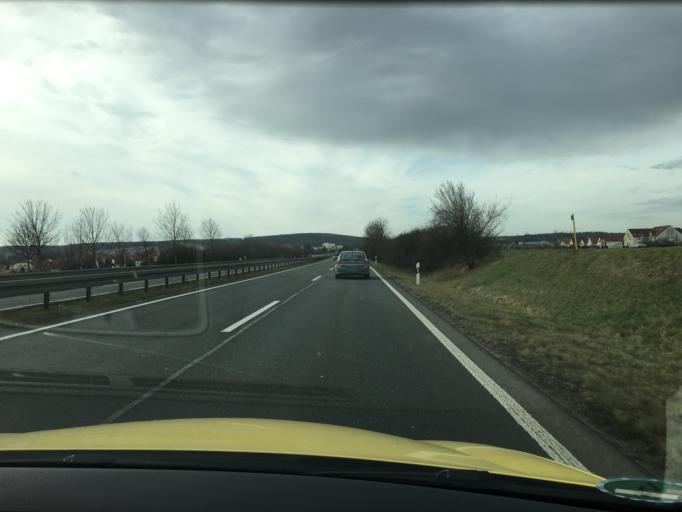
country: DE
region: Thuringia
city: Erfurt
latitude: 50.9679
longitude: 11.0902
